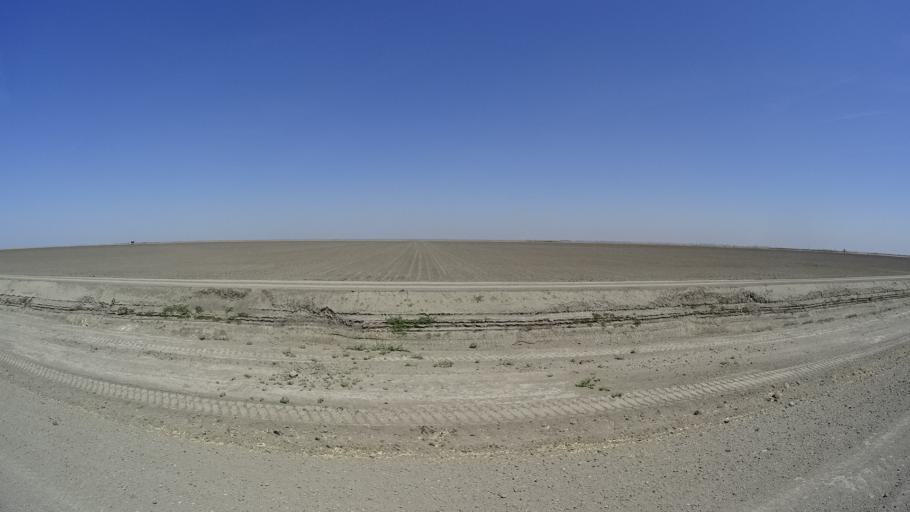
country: US
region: California
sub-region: Kings County
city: Corcoran
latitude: 36.0215
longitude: -119.6252
